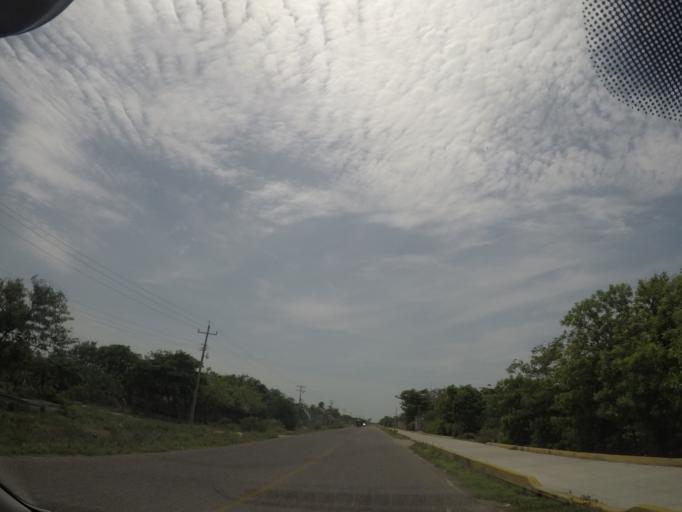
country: MX
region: Oaxaca
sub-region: San Mateo del Mar
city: Colonia Juarez
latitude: 16.2088
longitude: -95.0367
